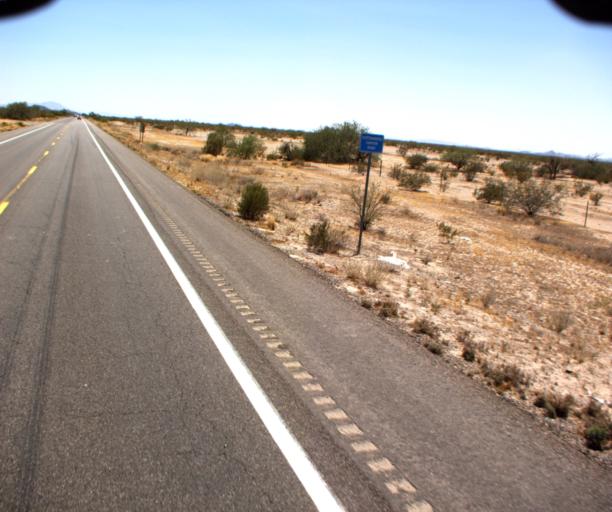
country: US
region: Arizona
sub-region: Pinal County
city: Gold Camp
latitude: 33.1804
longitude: -111.3519
